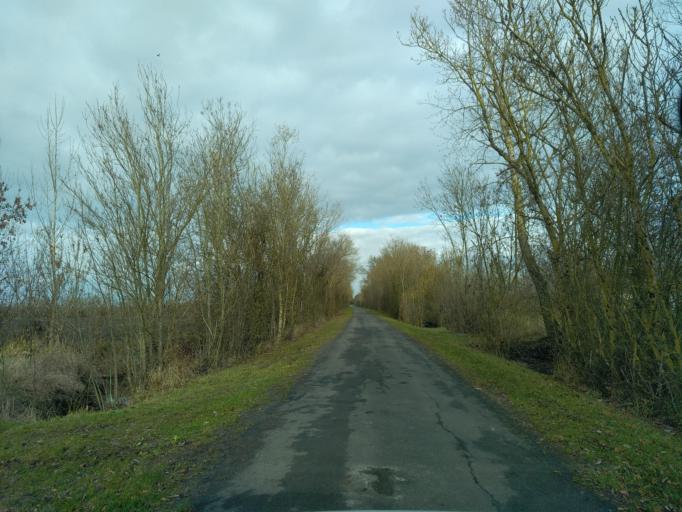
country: FR
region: Pays de la Loire
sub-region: Departement de la Vendee
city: Maillezais
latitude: 46.3309
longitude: -0.7922
